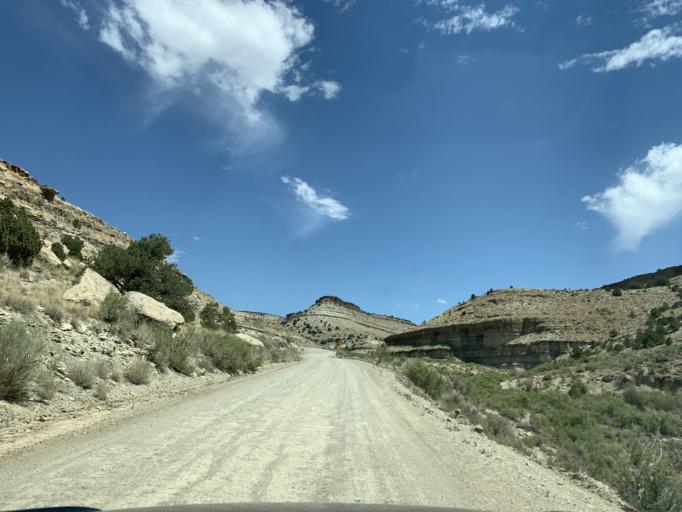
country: US
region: Utah
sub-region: Carbon County
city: East Carbon City
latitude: 39.8448
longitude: -110.2519
